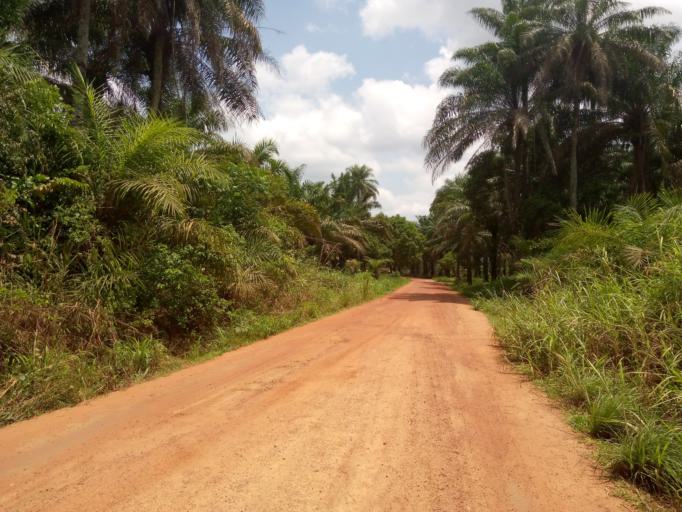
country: SL
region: Western Area
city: Waterloo
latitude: 8.3797
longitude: -12.9678
